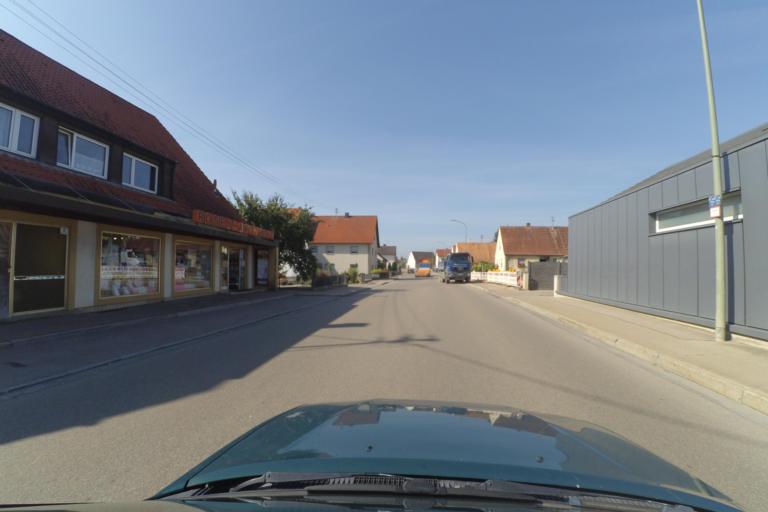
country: DE
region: Bavaria
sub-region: Swabia
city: Tapfheim
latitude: 48.6765
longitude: 10.6886
